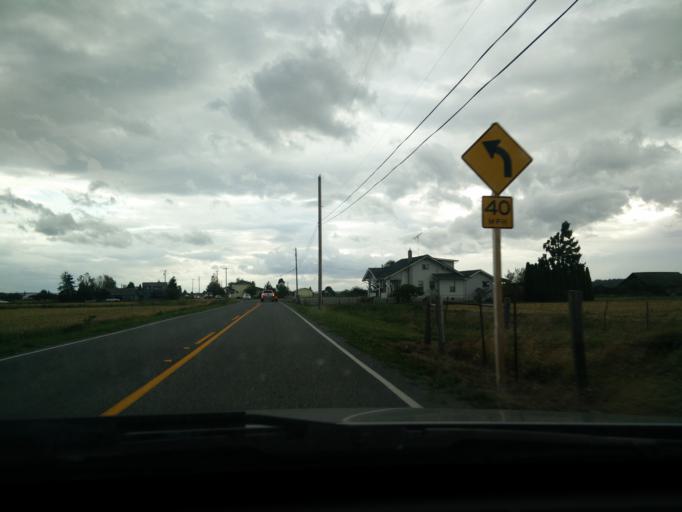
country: US
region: Washington
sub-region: Snohomish County
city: Stanwood
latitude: 48.2589
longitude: -122.3704
